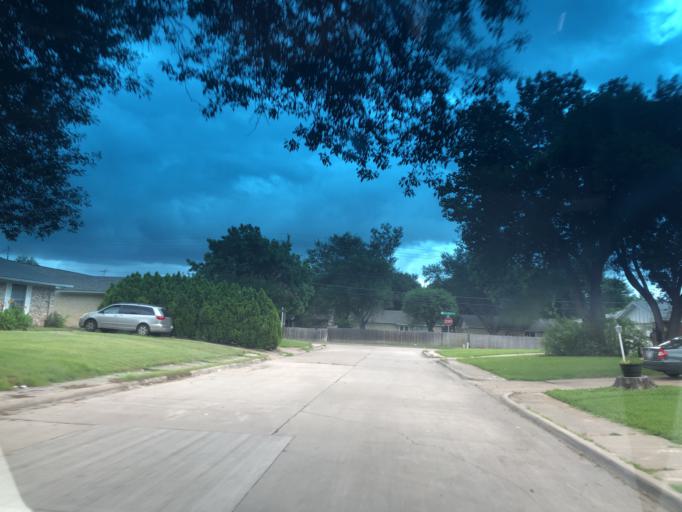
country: US
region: Texas
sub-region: Dallas County
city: Grand Prairie
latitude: 32.7049
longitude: -97.0032
